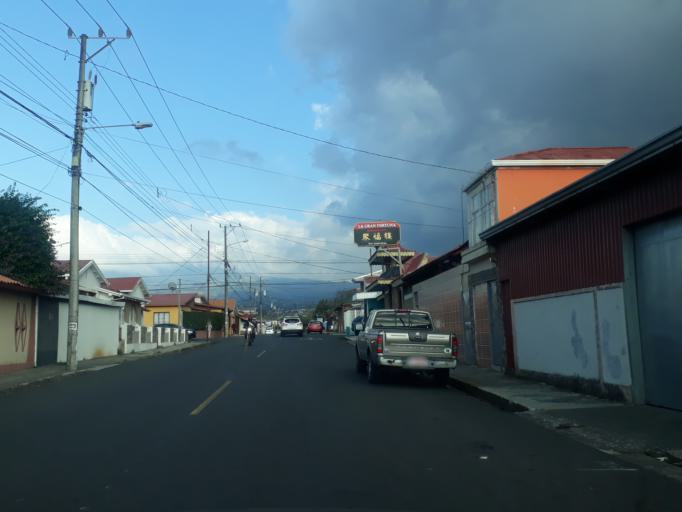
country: CR
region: San Jose
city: San Vicente
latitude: 9.9609
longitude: -84.0459
